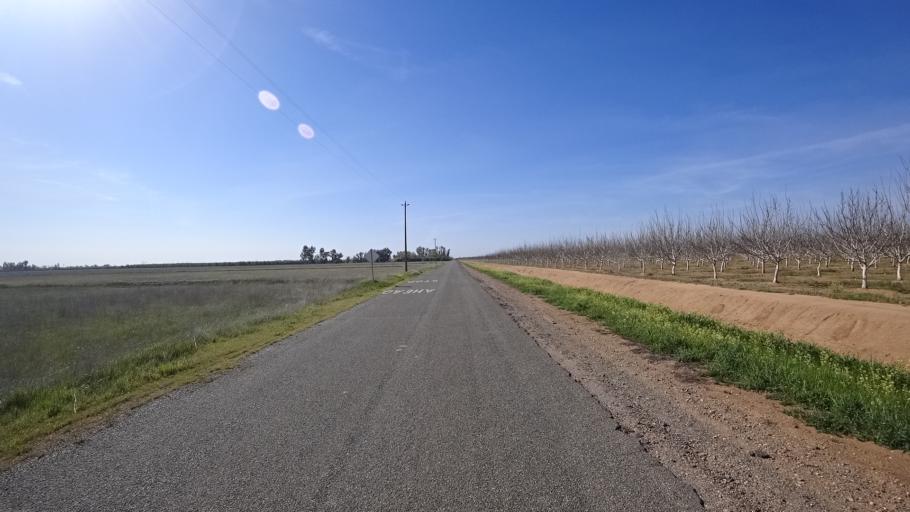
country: US
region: California
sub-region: Glenn County
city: Willows
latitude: 39.6229
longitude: -122.2130
